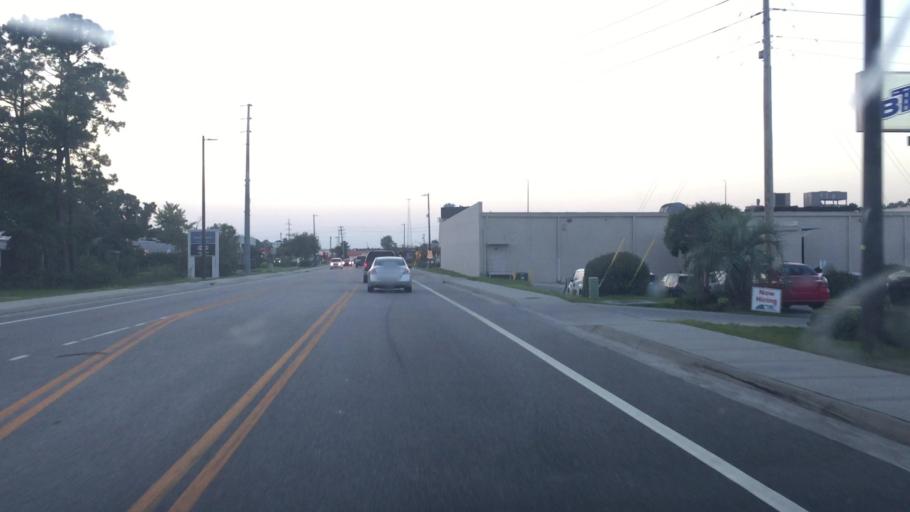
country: US
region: South Carolina
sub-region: Horry County
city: Myrtle Beach
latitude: 33.6960
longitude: -78.8982
